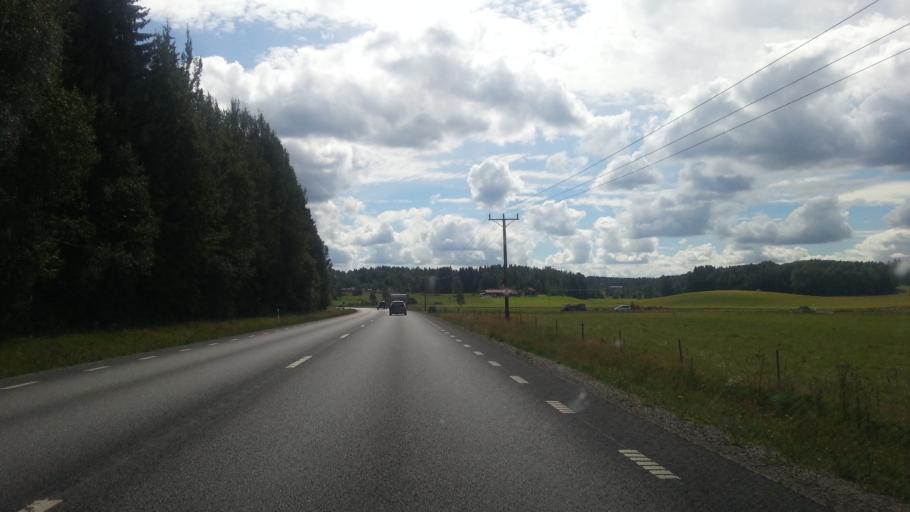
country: SE
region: OErebro
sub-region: Lindesbergs Kommun
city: Lindesberg
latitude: 59.5745
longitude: 15.2056
